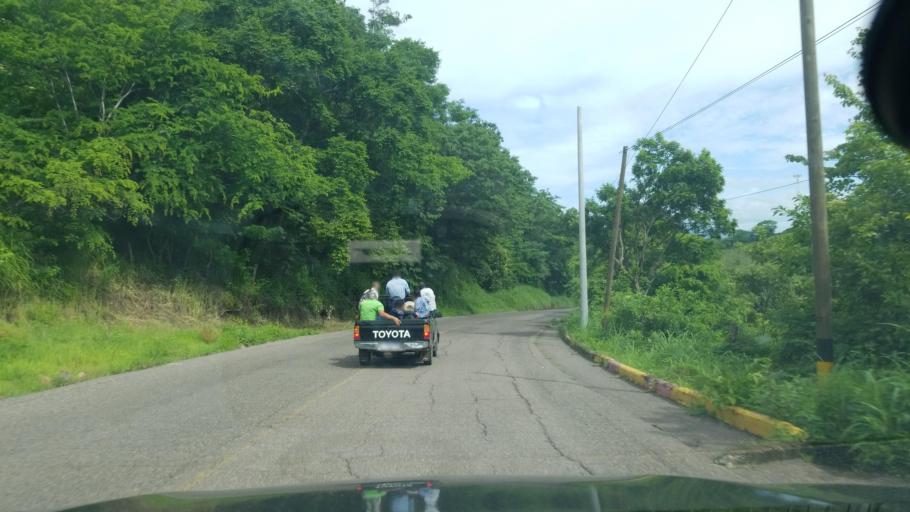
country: HN
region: Choluteca
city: Corpus
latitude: 13.3733
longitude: -87.0427
